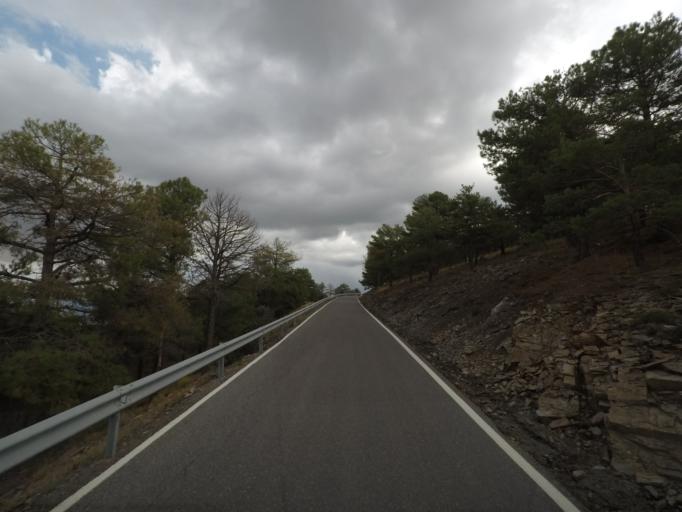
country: ES
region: Andalusia
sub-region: Provincia de Granada
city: Aldeire
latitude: 37.1595
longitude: -3.0526
